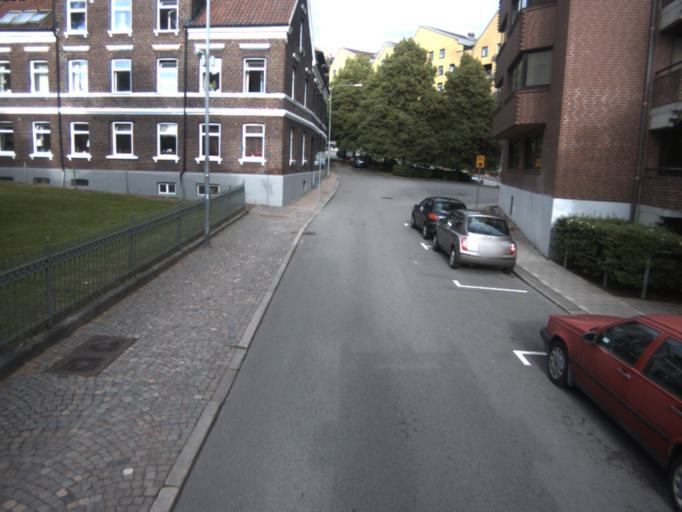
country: SE
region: Skane
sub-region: Helsingborg
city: Helsingborg
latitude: 56.0416
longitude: 12.7026
